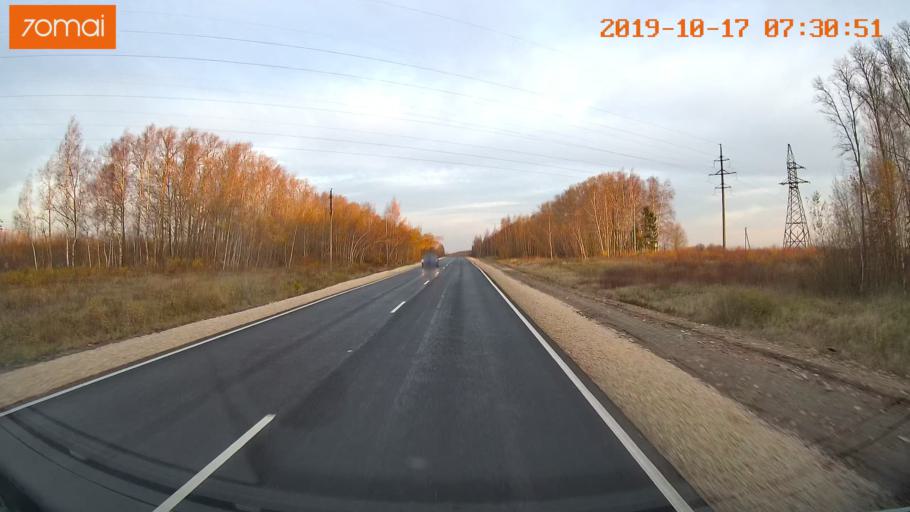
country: RU
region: Ivanovo
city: Gavrilov Posad
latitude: 56.3816
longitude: 40.0049
